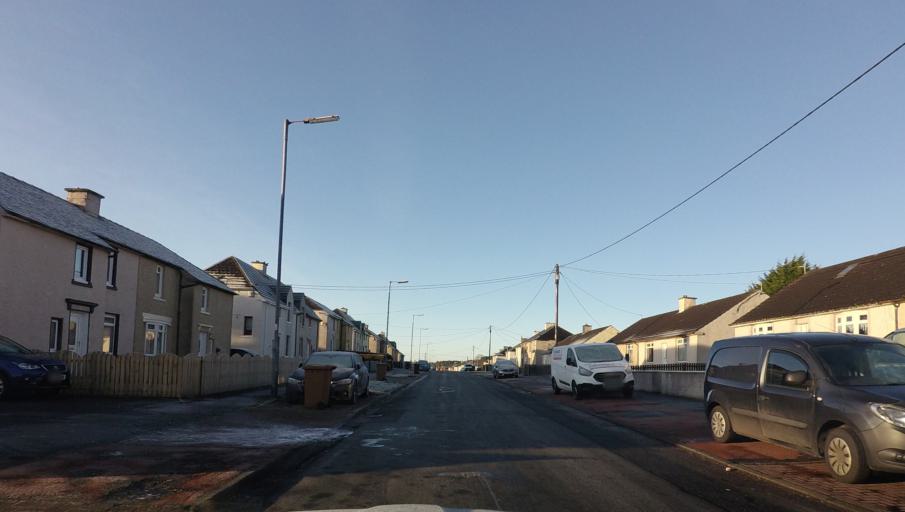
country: GB
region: Scotland
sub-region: North Lanarkshire
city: Shotts
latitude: 55.8241
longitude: -3.8031
